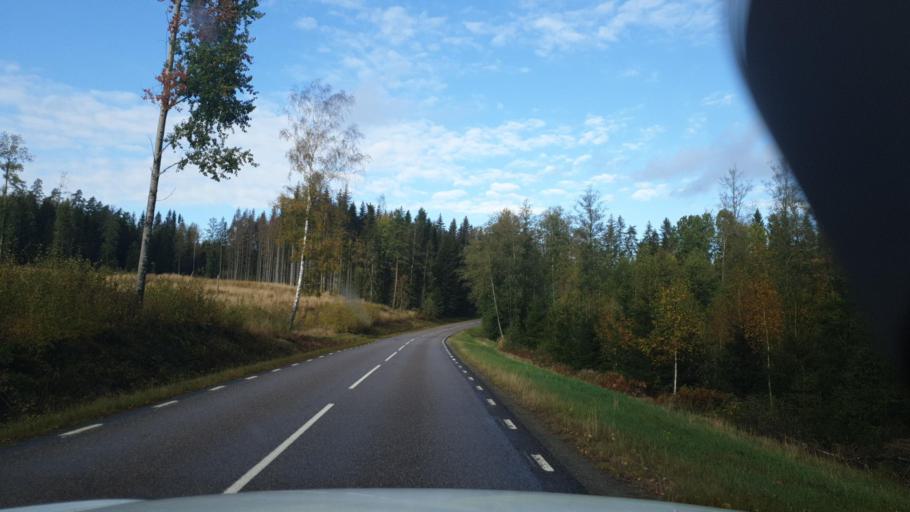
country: SE
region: Vaermland
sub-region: Arvika Kommun
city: Arvika
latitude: 59.4674
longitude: 12.7355
